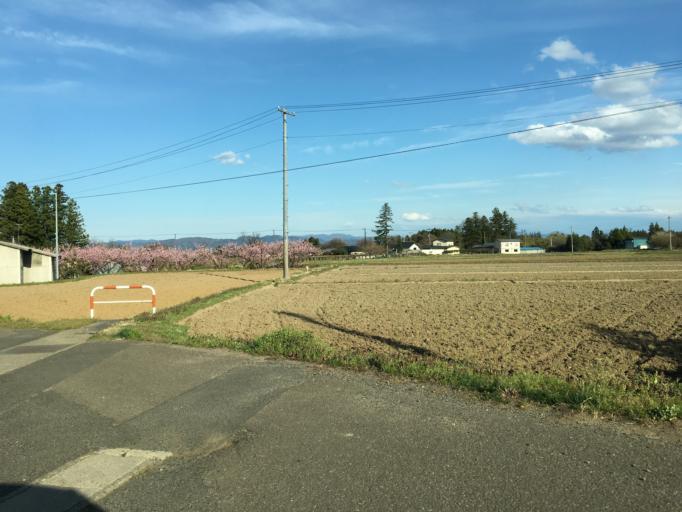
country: JP
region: Fukushima
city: Fukushima-shi
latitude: 37.7544
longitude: 140.3695
